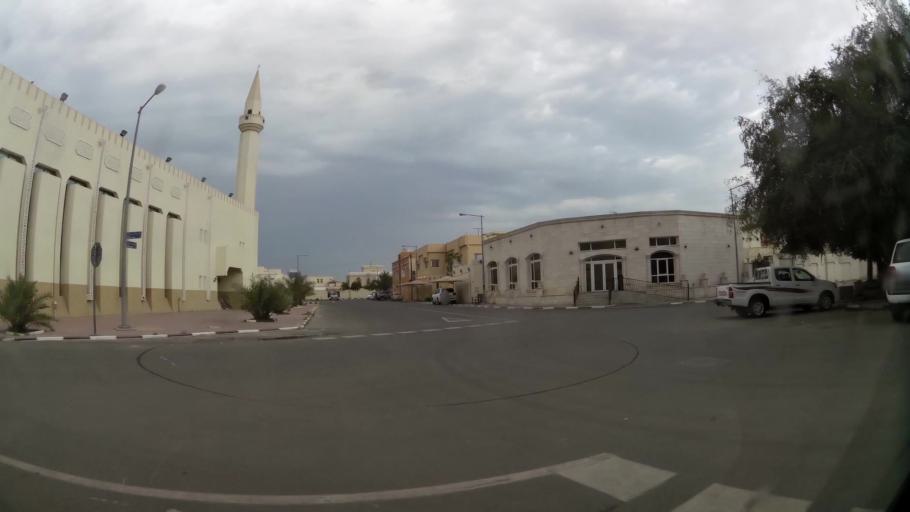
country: QA
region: Baladiyat ad Dawhah
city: Doha
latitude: 25.2701
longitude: 51.4979
